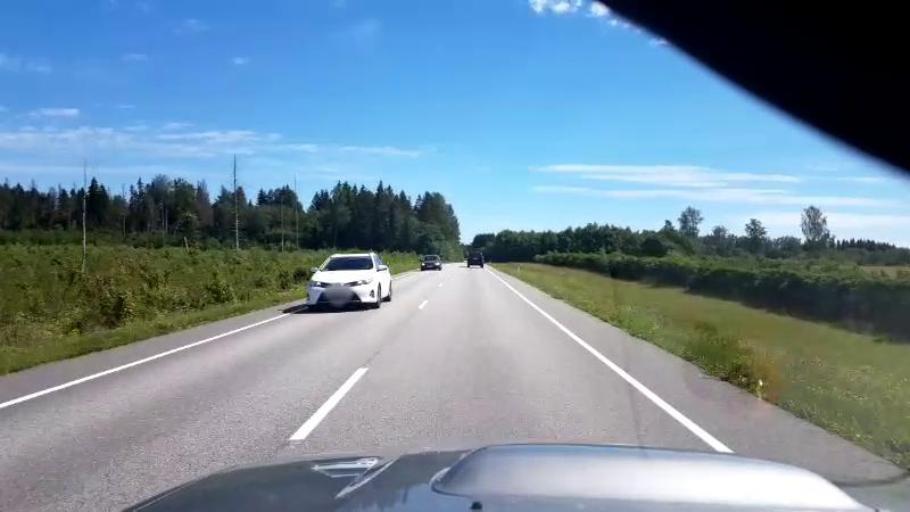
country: EE
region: Jaervamaa
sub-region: Jaerva-Jaani vald
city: Jarva-Jaani
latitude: 59.0187
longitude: 25.9064
